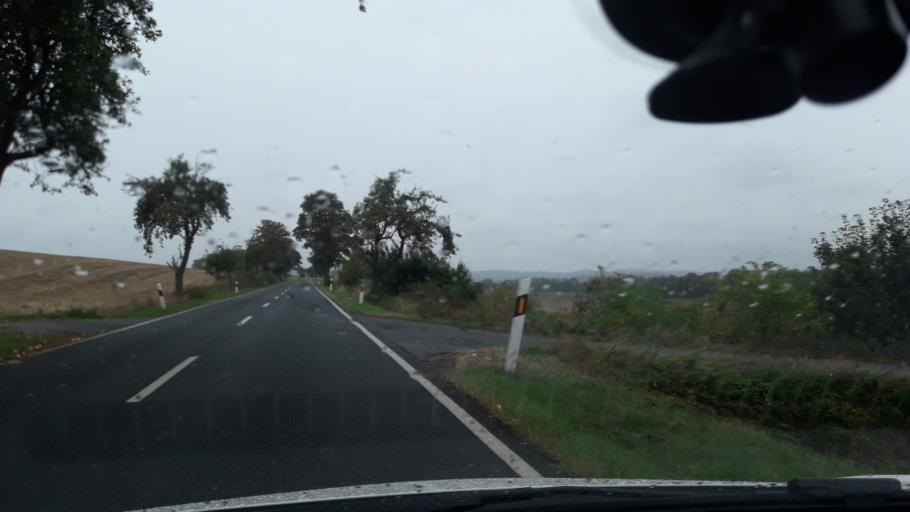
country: DE
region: Lower Saxony
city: Schladen
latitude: 52.0016
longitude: 10.5342
